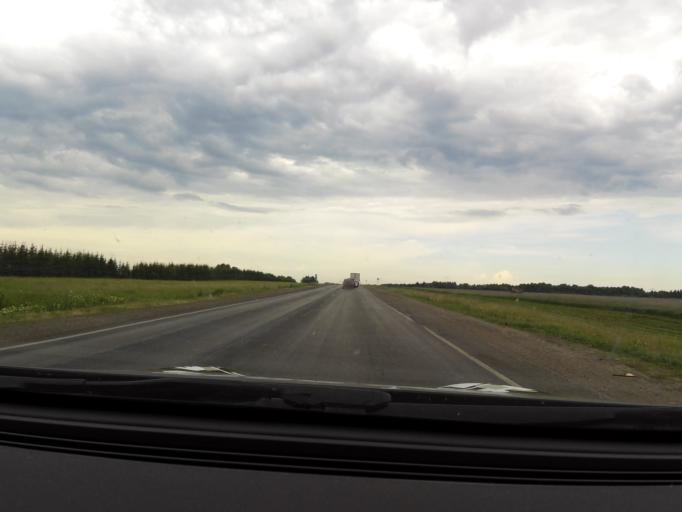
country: RU
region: Bashkortostan
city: Kudeyevskiy
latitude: 54.8167
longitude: 56.7263
